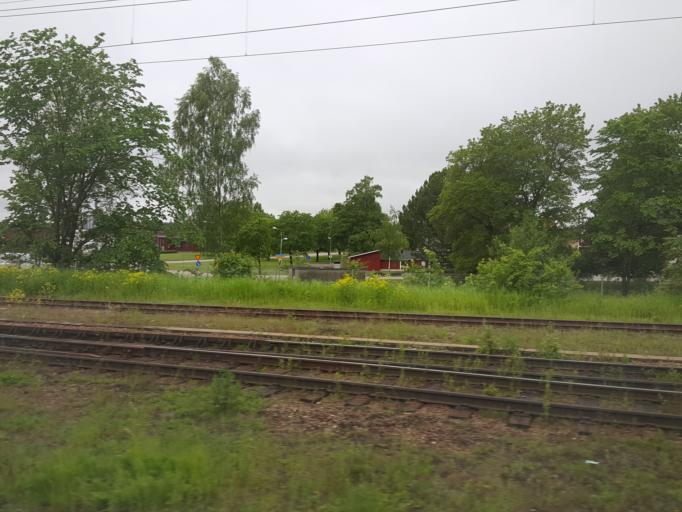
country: SE
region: Dalarna
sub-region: Avesta Kommun
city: Avesta
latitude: 60.1251
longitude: 16.2187
